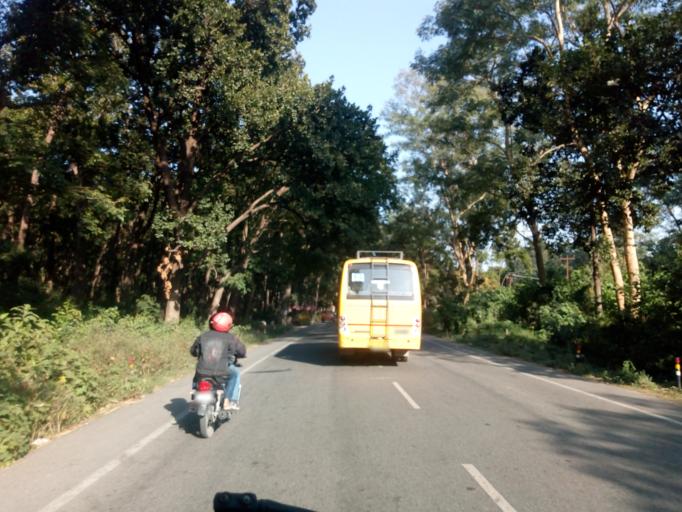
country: IN
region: Uttarakhand
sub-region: Dehradun
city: Dehradun
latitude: 30.3470
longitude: 77.8778
